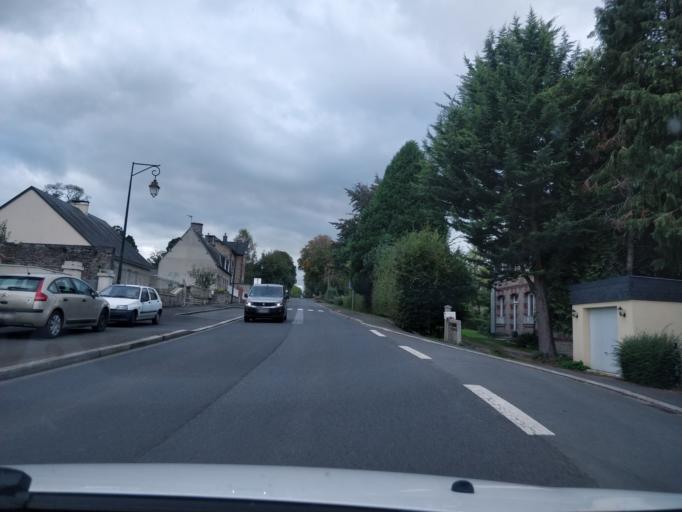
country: FR
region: Lower Normandy
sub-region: Departement du Calvados
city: Saint-Sever-Calvados
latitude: 48.8395
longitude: -1.0546
